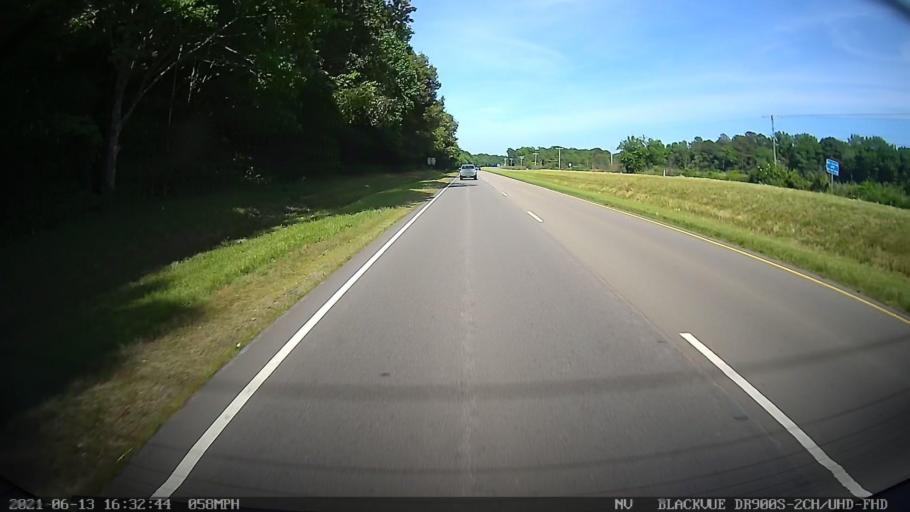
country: US
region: Virginia
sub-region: City of Hopewell
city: Hopewell
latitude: 37.2852
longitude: -77.2367
